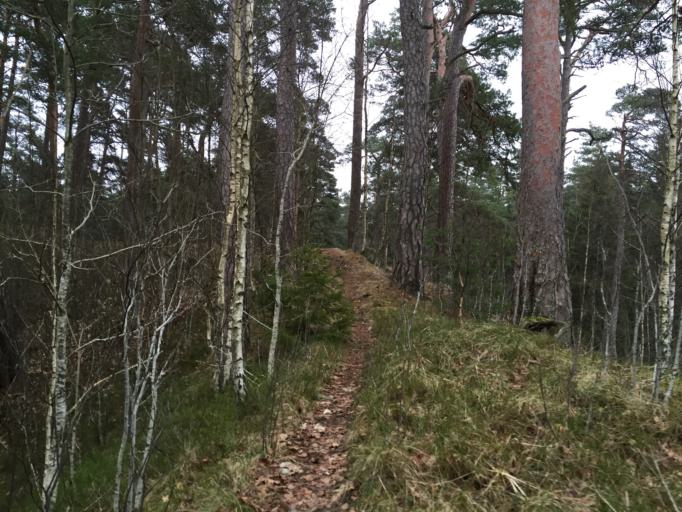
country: EE
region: Saare
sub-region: Kuressaare linn
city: Kuressaare
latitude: 58.3989
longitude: 22.2524
